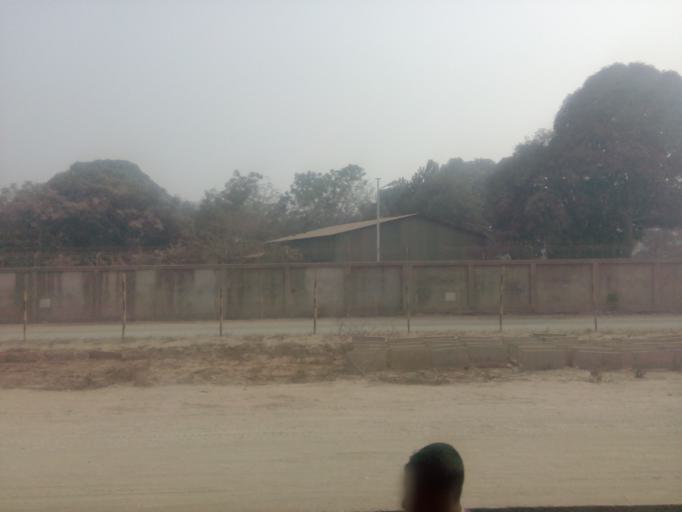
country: BD
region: Dhaka
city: Narayanganj
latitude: 23.6129
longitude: 90.6112
